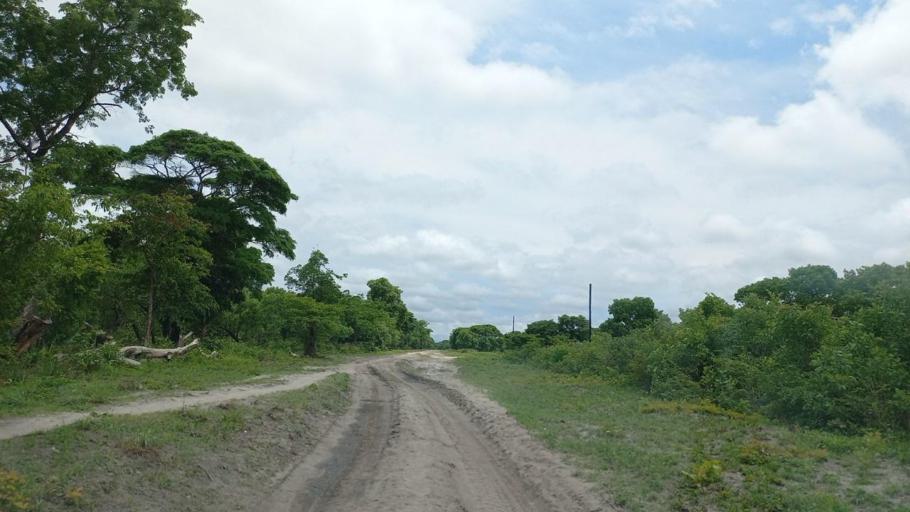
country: ZM
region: North-Western
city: Kabompo
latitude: -13.1853
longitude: 23.9540
